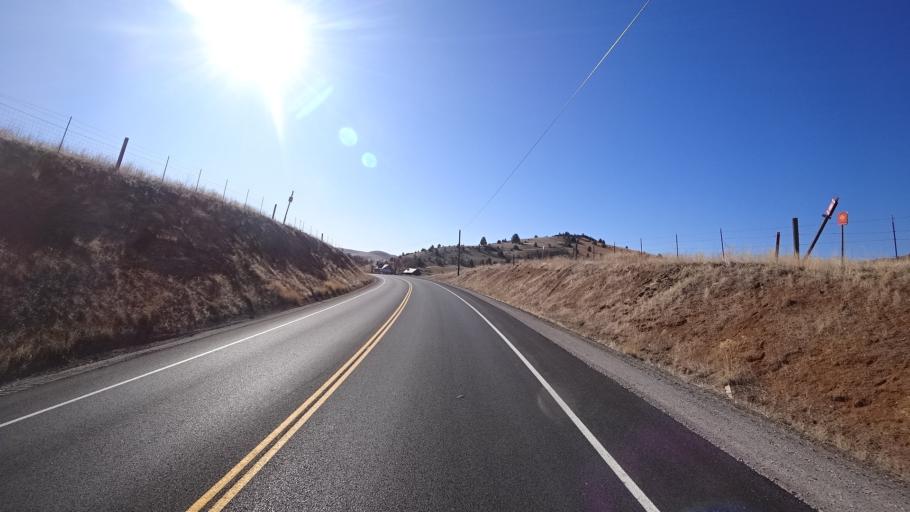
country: US
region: California
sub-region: Siskiyou County
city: Montague
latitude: 41.8567
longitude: -122.4656
